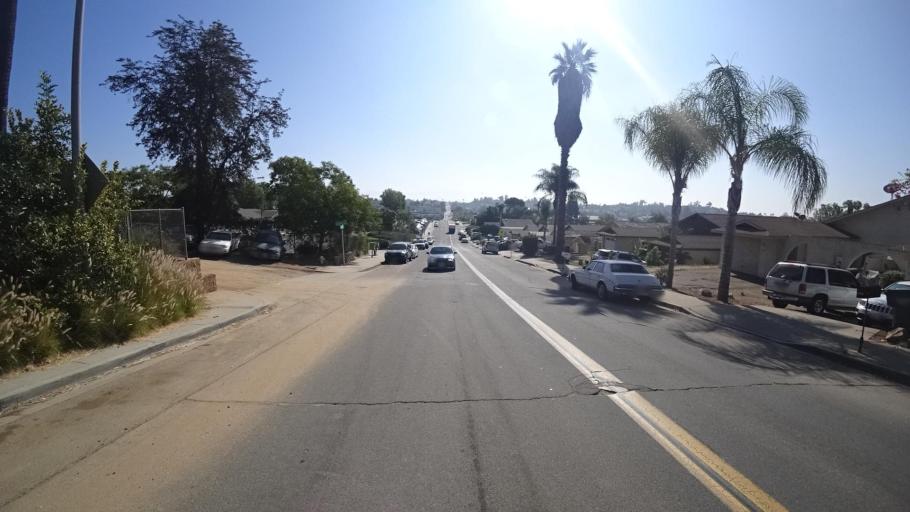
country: US
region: California
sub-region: San Diego County
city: Fallbrook
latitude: 33.3768
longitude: -117.2570
